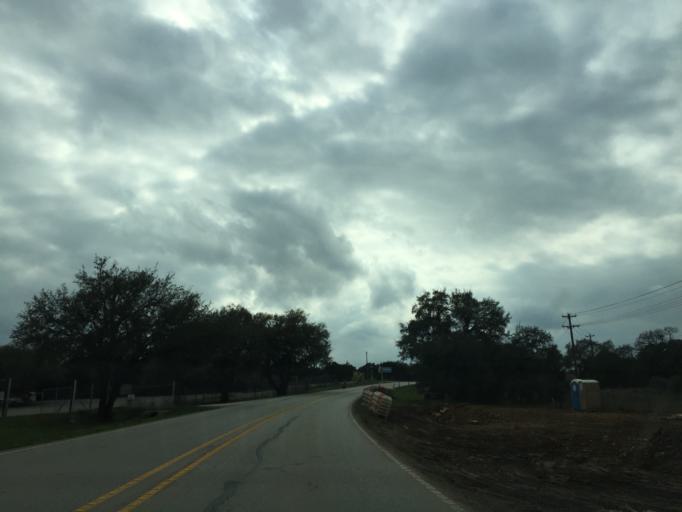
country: US
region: Texas
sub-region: Travis County
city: Shady Hollow
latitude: 30.1589
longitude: -97.9561
